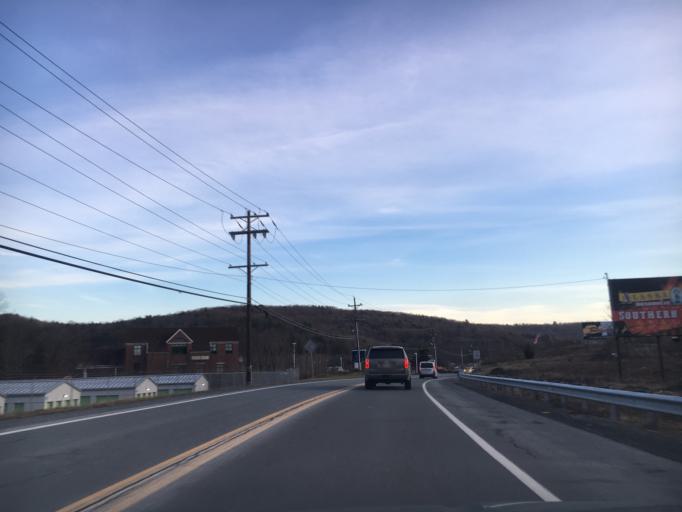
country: US
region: Pennsylvania
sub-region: Monroe County
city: East Stroudsburg
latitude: 41.0403
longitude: -75.1271
